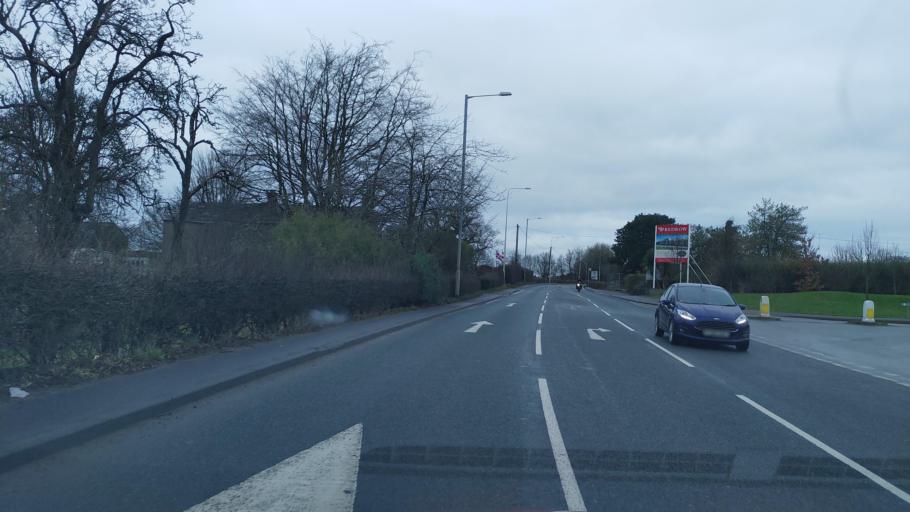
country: GB
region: England
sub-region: Lancashire
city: Clayton-le-Woods
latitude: 53.7024
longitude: -2.6733
